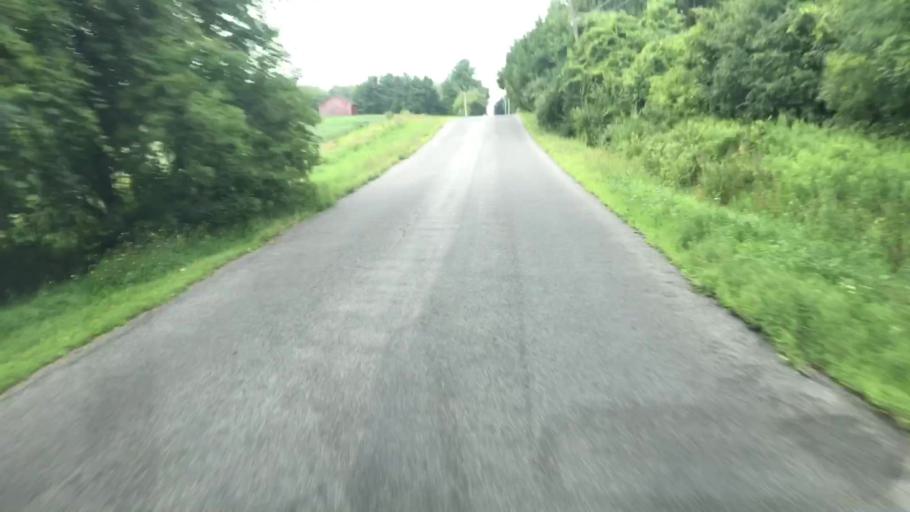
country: US
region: New York
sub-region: Cayuga County
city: Melrose Park
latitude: 42.9549
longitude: -76.5066
